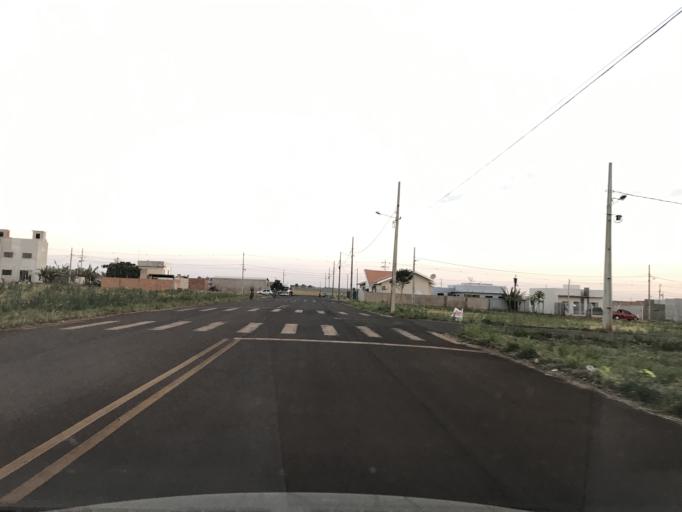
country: BR
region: Parana
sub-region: Palotina
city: Palotina
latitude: -24.3071
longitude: -53.8365
